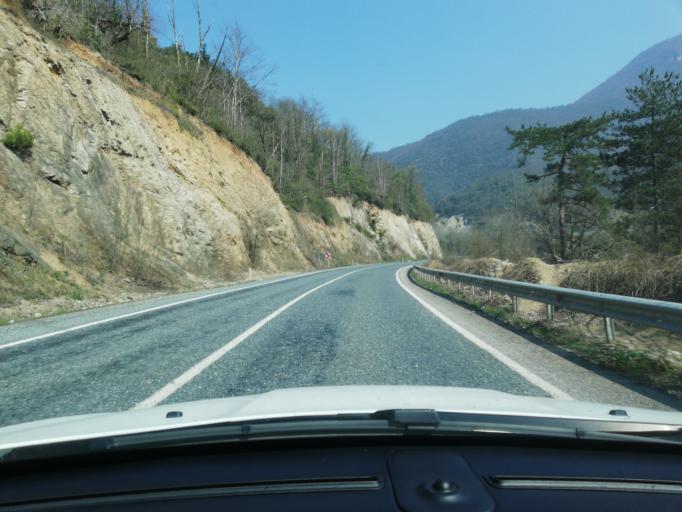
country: TR
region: Zonguldak
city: Gokcebey
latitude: 41.2493
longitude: 32.1667
